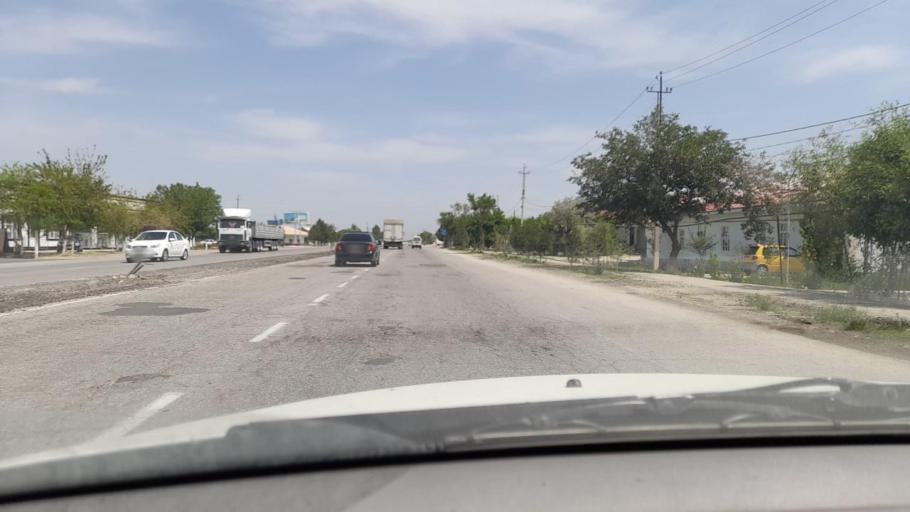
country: UZ
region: Navoiy
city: Beshrabot
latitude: 40.1437
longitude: 65.2996
